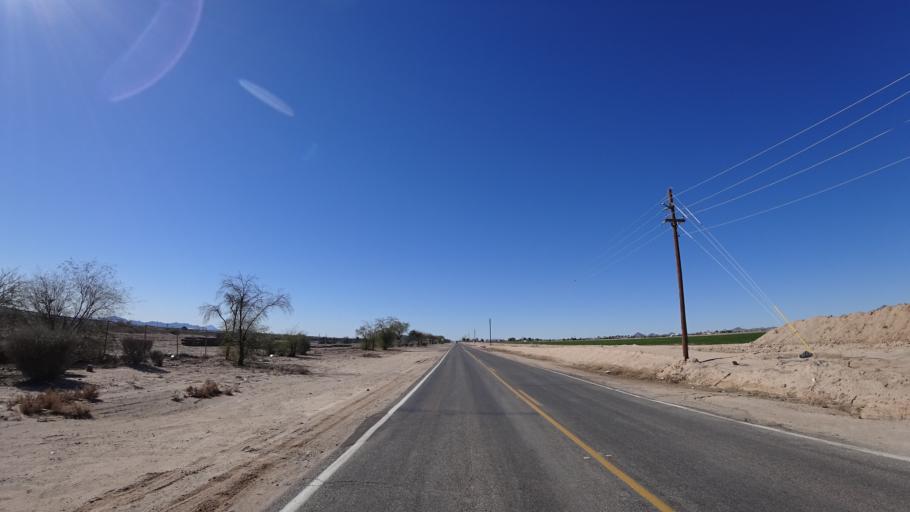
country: US
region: Arizona
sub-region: Maricopa County
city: Buckeye
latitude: 33.3922
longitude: -112.5217
